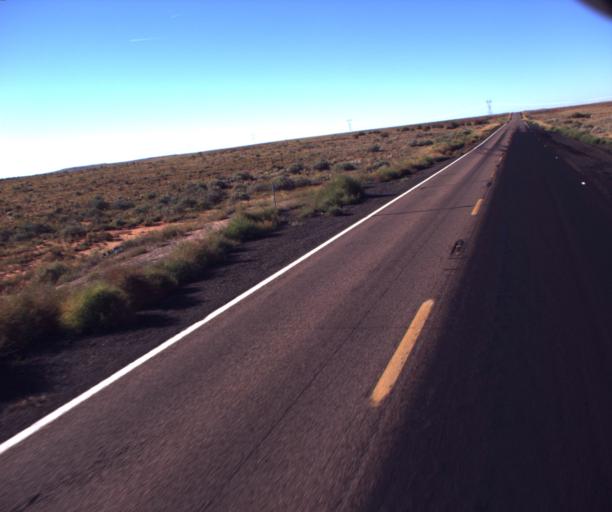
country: US
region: Arizona
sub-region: Navajo County
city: Holbrook
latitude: 34.8050
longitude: -110.2068
